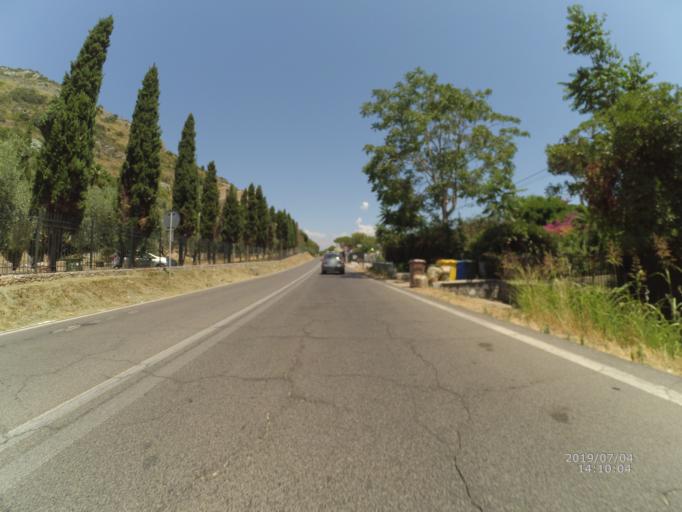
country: IT
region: Latium
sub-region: Provincia di Latina
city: Terracina
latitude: 41.2973
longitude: 13.2724
